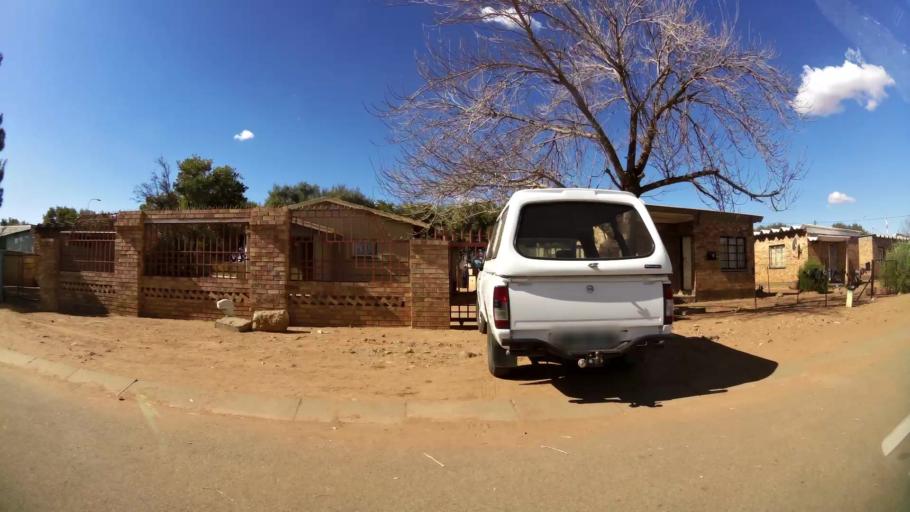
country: ZA
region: North-West
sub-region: Dr Kenneth Kaunda District Municipality
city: Klerksdorp
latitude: -26.8715
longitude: 26.5885
